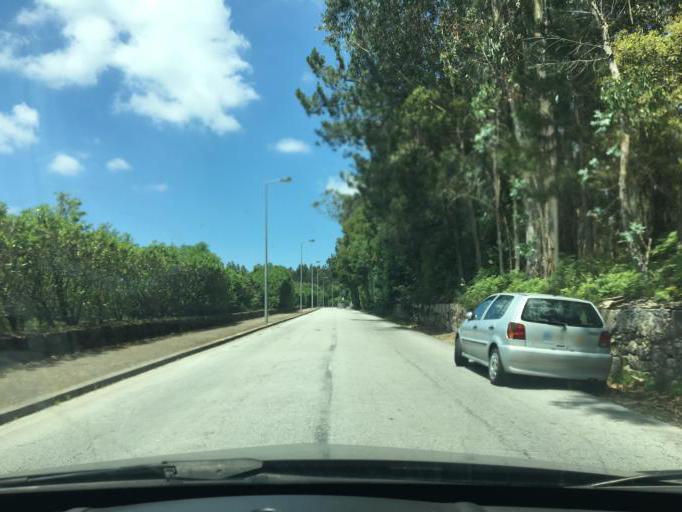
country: PT
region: Porto
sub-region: Maia
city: Anta
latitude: 41.2912
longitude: -8.6112
